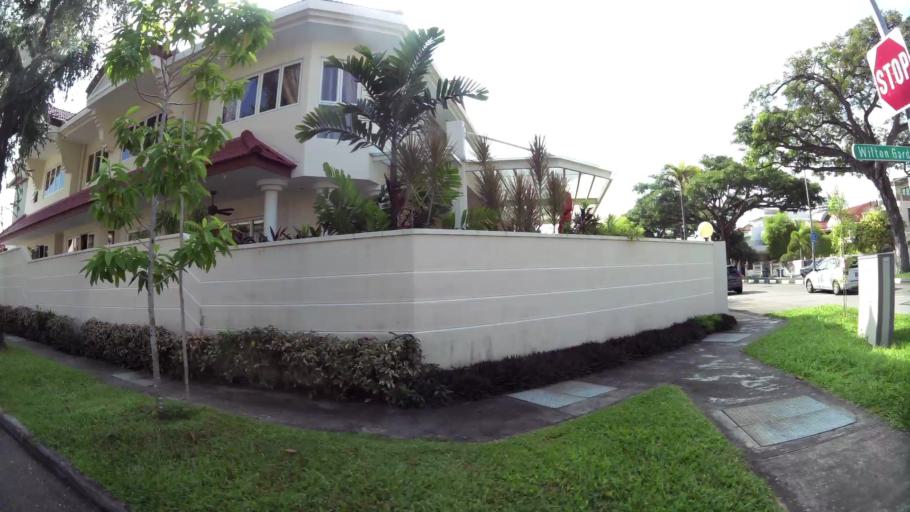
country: SG
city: Singapore
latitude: 1.3137
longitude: 103.9196
